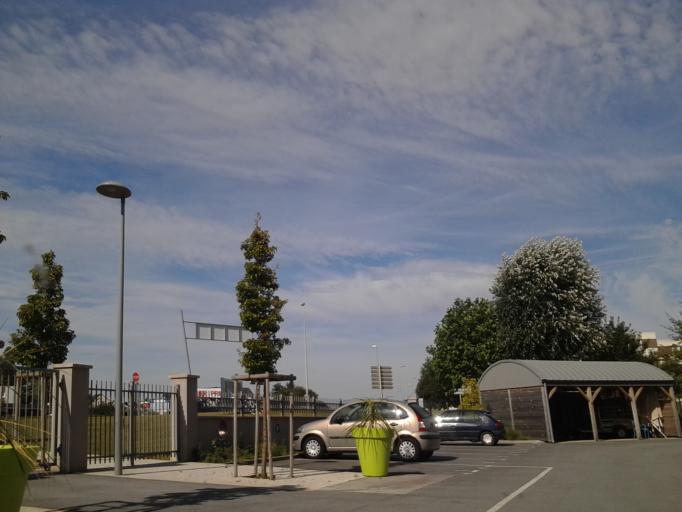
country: FR
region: Lower Normandy
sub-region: Departement de la Manche
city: Tourlaville
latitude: 49.6443
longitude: -1.5804
